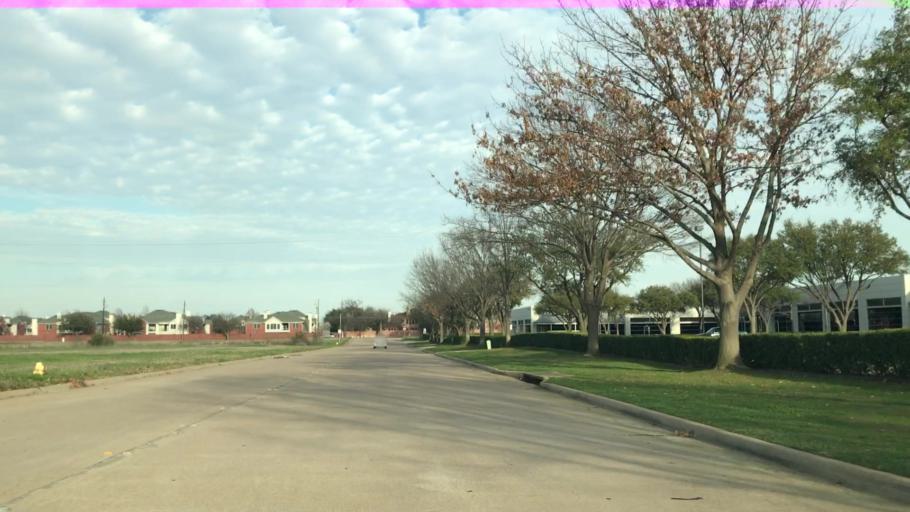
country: US
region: Texas
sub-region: Dallas County
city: Coppell
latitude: 32.9819
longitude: -97.0138
